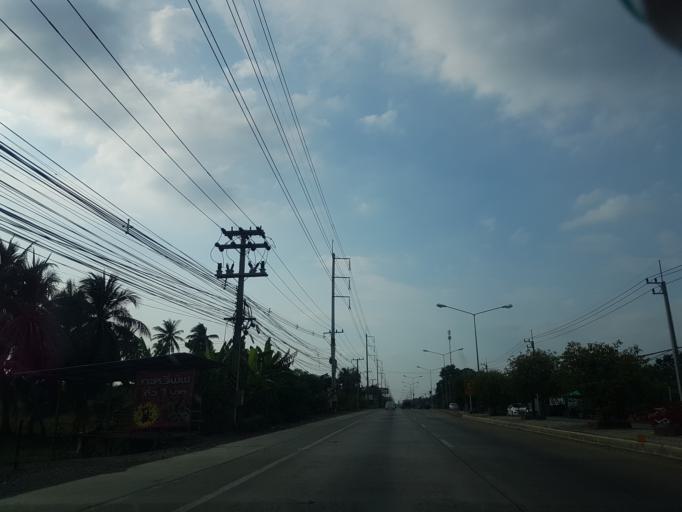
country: TH
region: Sara Buri
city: Nong Don
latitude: 14.7606
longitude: 100.7237
